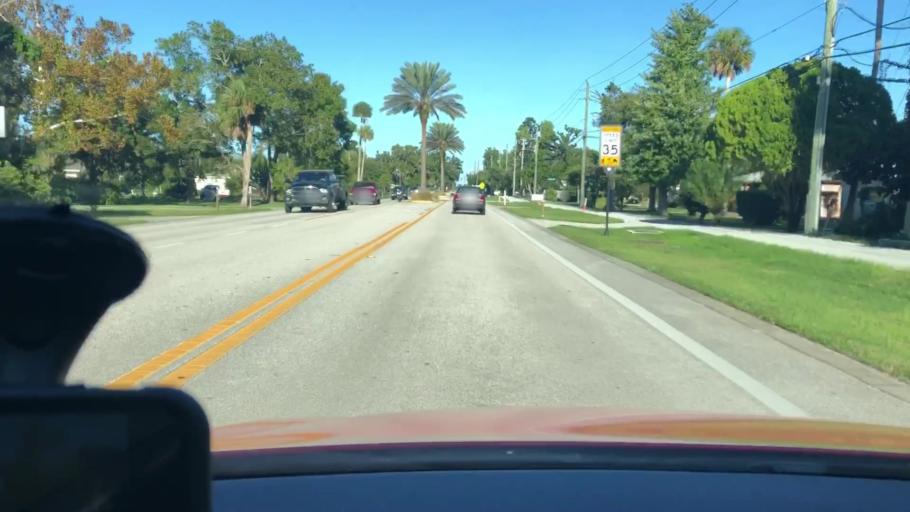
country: US
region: Florida
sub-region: Volusia County
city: South Daytona
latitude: 29.1699
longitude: -81.0144
